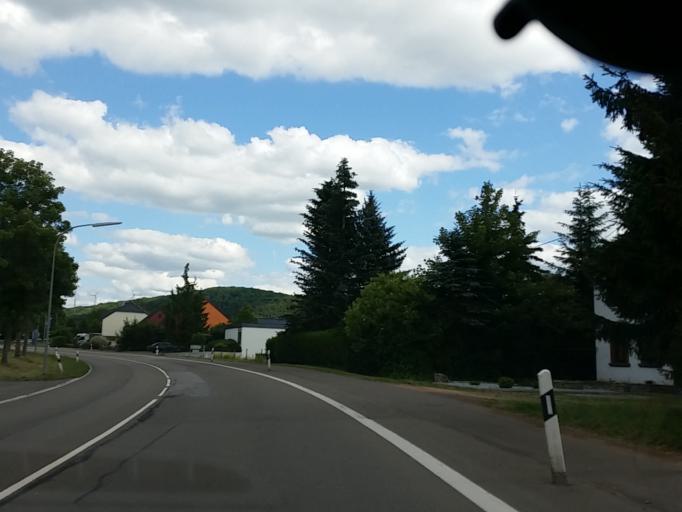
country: DE
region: Saarland
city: Wadern
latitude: 49.5272
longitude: 6.9024
